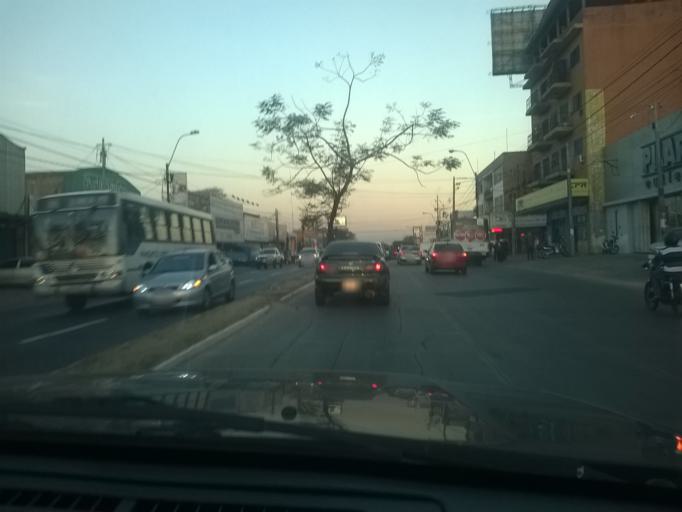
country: PY
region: Asuncion
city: Asuncion
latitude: -25.3061
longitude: -57.6040
